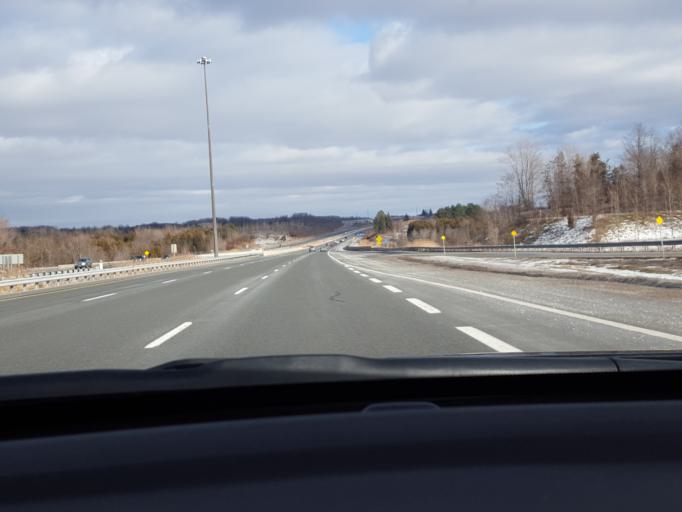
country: CA
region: Ontario
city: Markham
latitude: 43.8641
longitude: -79.2549
